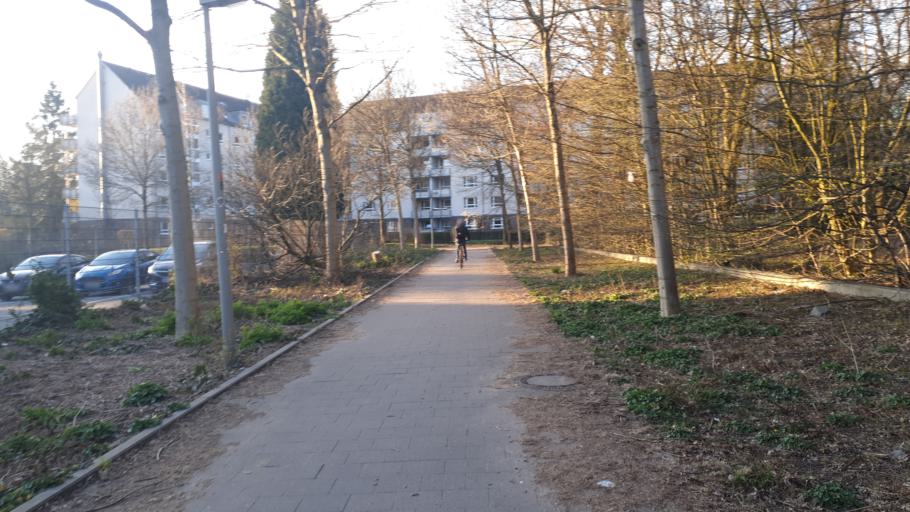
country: DE
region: Hamburg
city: Hamburg-Nord
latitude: 53.5859
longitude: 9.9651
